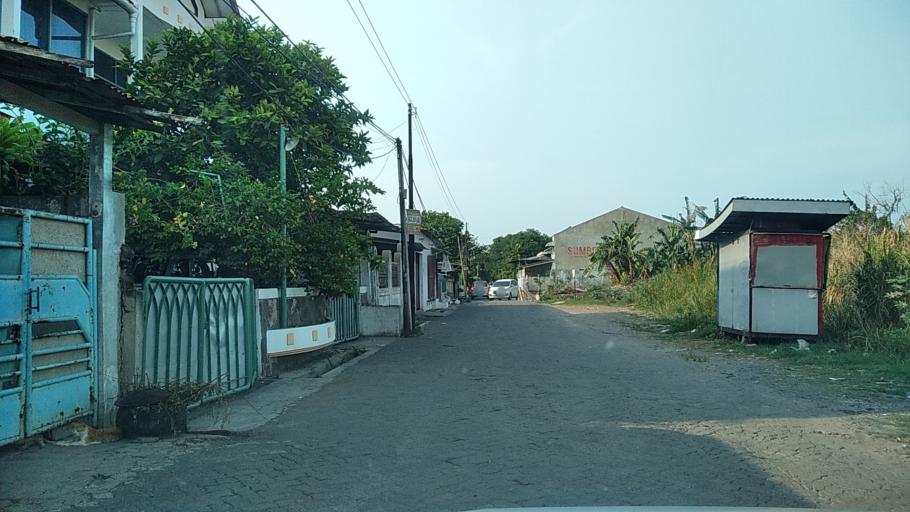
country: ID
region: Central Java
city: Semarang
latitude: -6.9583
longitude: 110.4075
